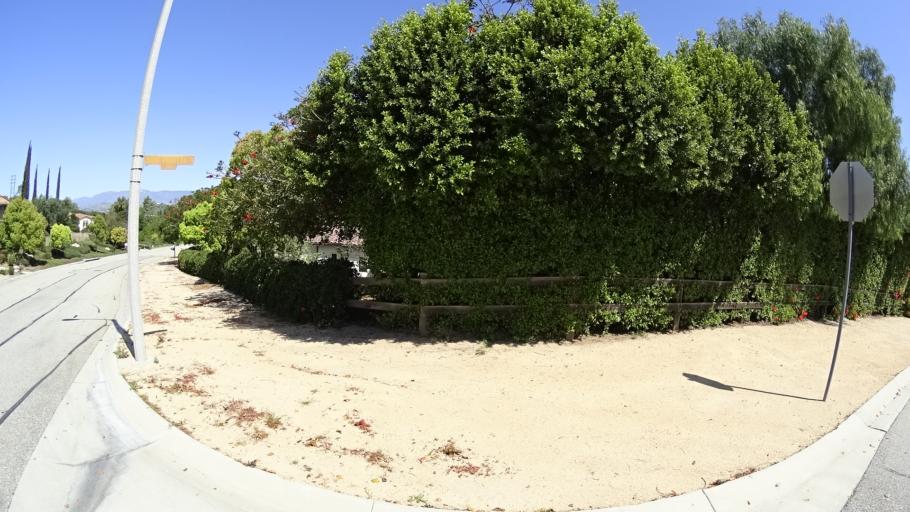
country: US
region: California
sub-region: Ventura County
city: Moorpark
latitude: 34.2470
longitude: -118.8430
